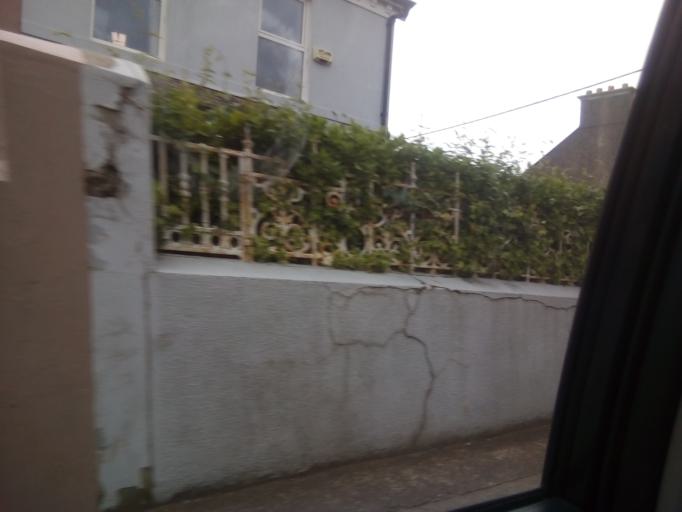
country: IE
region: Munster
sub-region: County Cork
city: Cork
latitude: 51.8900
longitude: -8.4942
